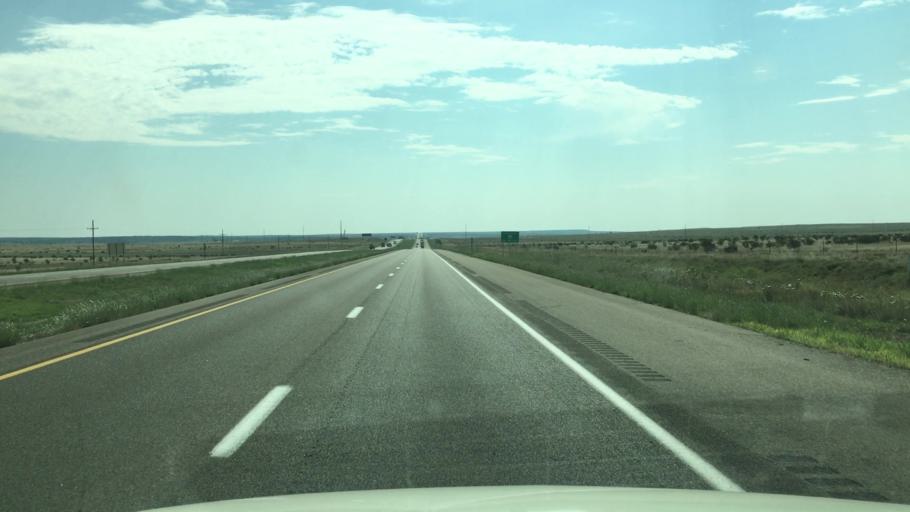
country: US
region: New Mexico
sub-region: Guadalupe County
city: Santa Rosa
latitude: 34.9786
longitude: -105.0372
